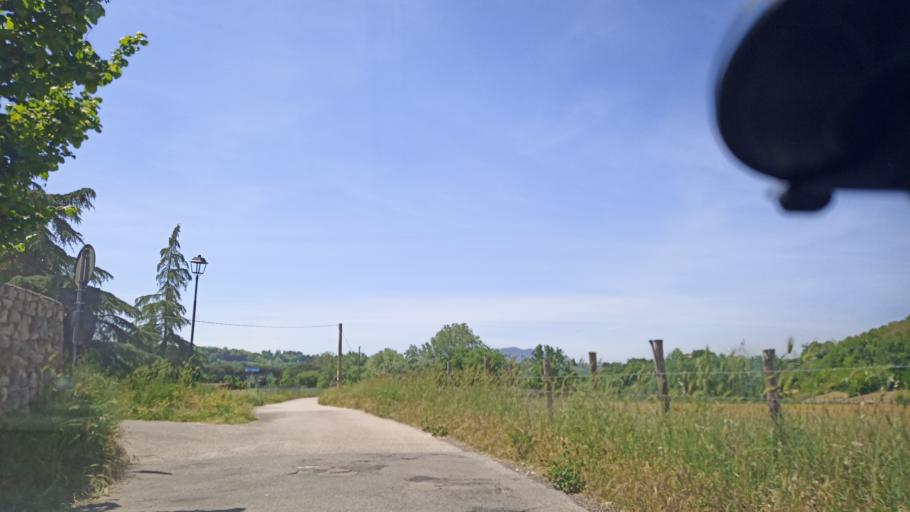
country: IT
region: Latium
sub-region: Provincia di Rieti
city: Tarano
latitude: 42.3316
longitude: 12.6040
